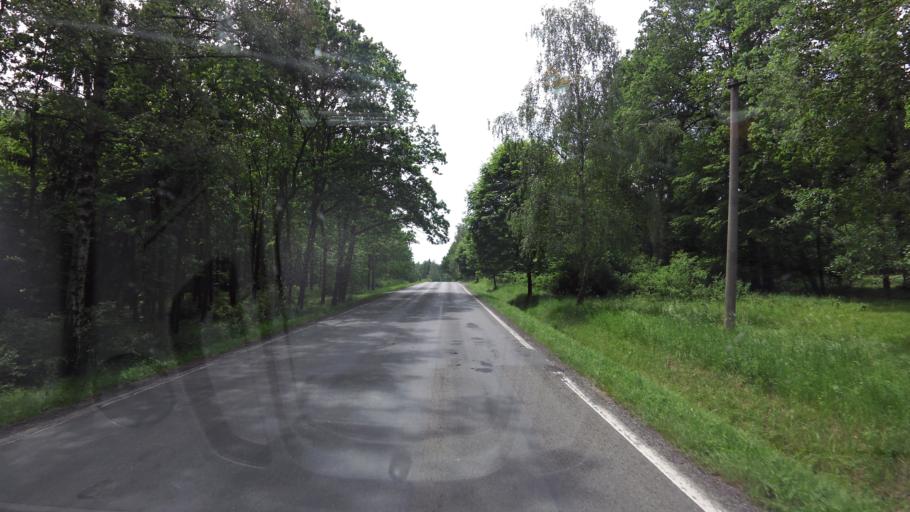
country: CZ
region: Plzensky
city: Holoubkov
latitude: 49.7672
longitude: 13.6711
